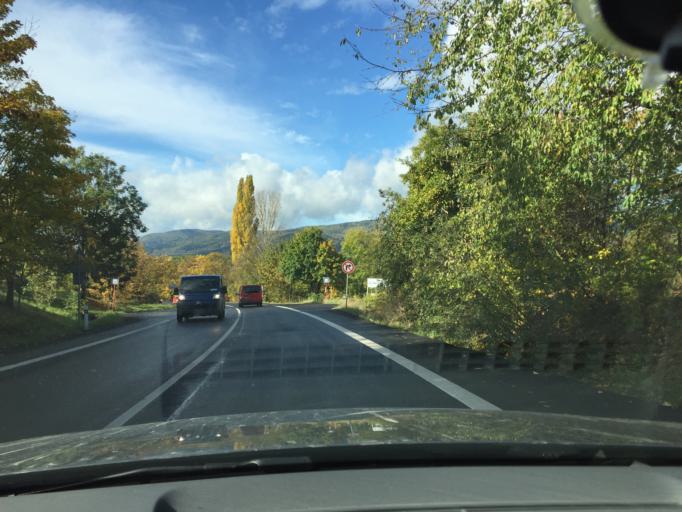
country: CZ
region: Ustecky
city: Chlumec
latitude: 50.6914
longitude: 13.9801
